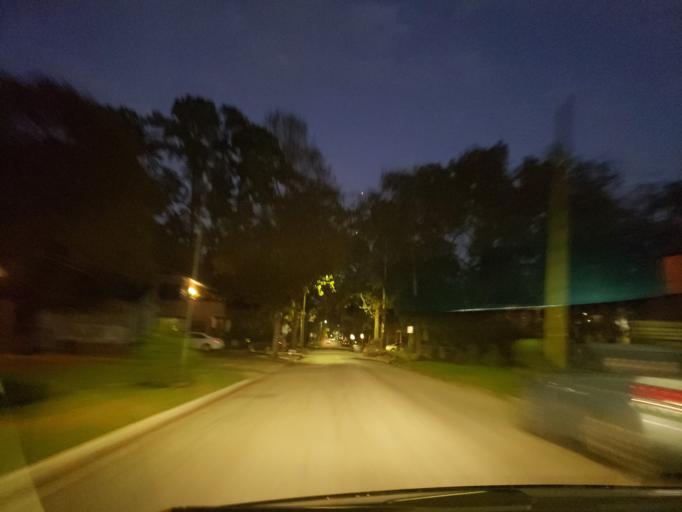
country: US
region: Georgia
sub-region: Chatham County
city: Thunderbolt
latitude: 32.0484
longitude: -81.0825
